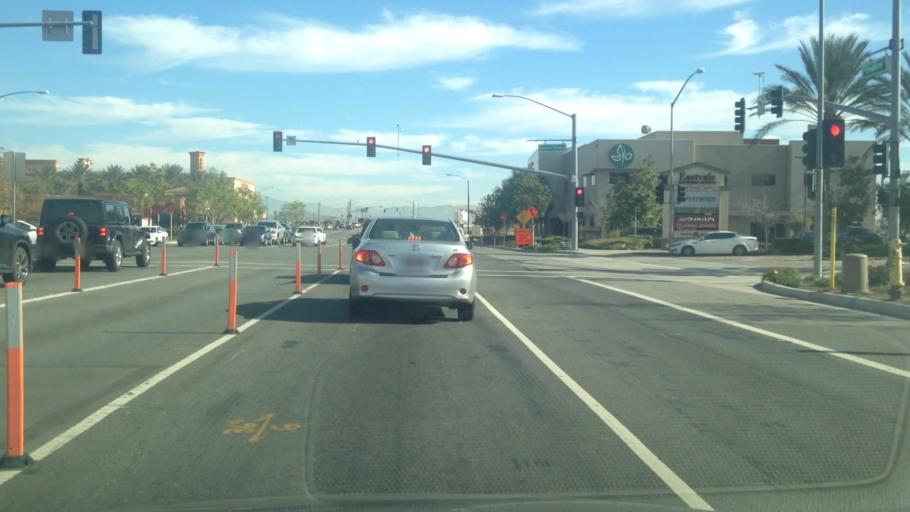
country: US
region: California
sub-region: Riverside County
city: Mira Loma
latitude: 33.9751
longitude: -117.5547
